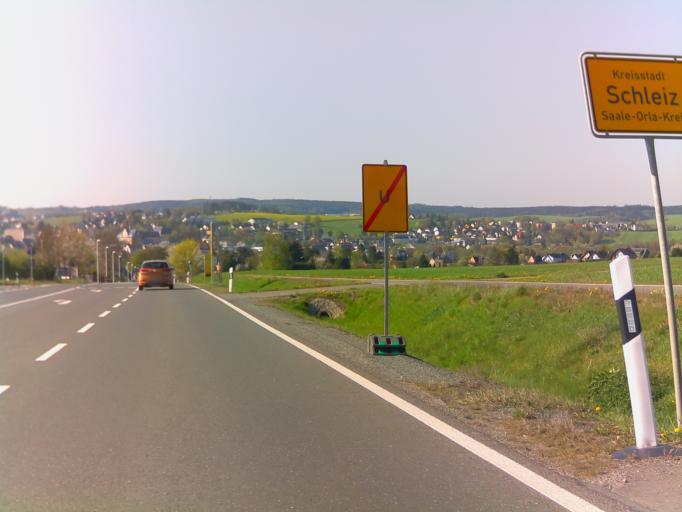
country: DE
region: Thuringia
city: Schleiz
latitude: 50.5894
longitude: 11.8124
